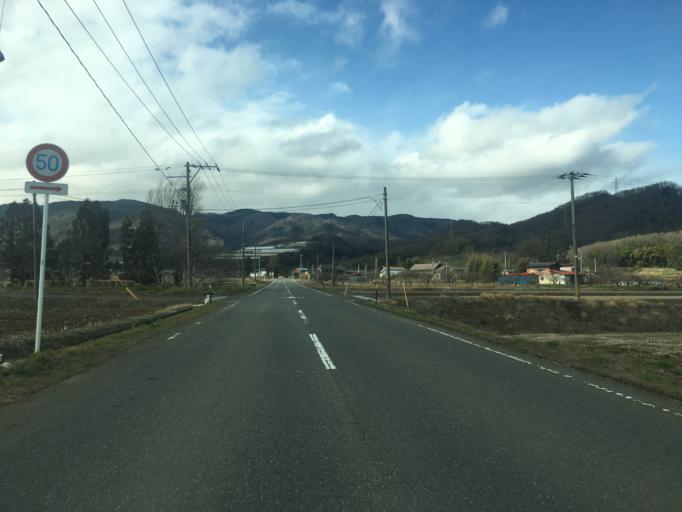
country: JP
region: Fukushima
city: Yanagawamachi-saiwaicho
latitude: 37.8863
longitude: 140.5898
